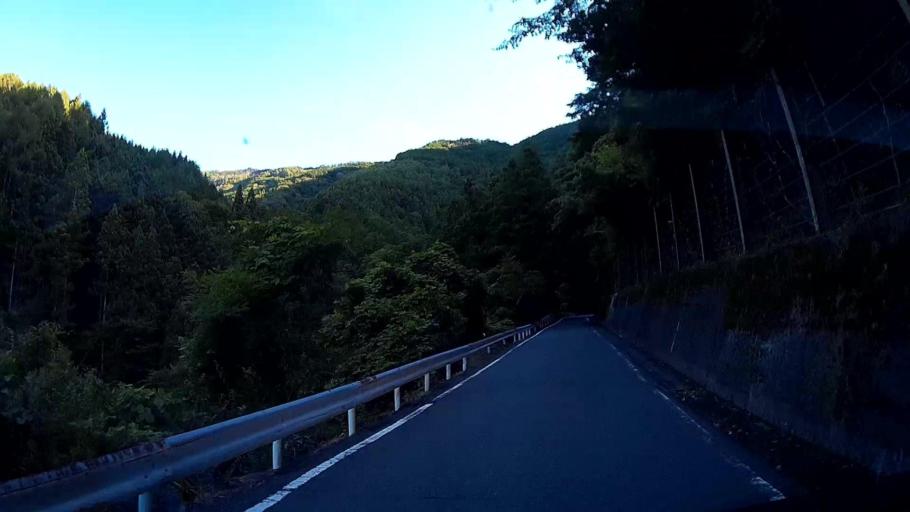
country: JP
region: Shizuoka
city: Shizuoka-shi
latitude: 35.1923
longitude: 138.2397
